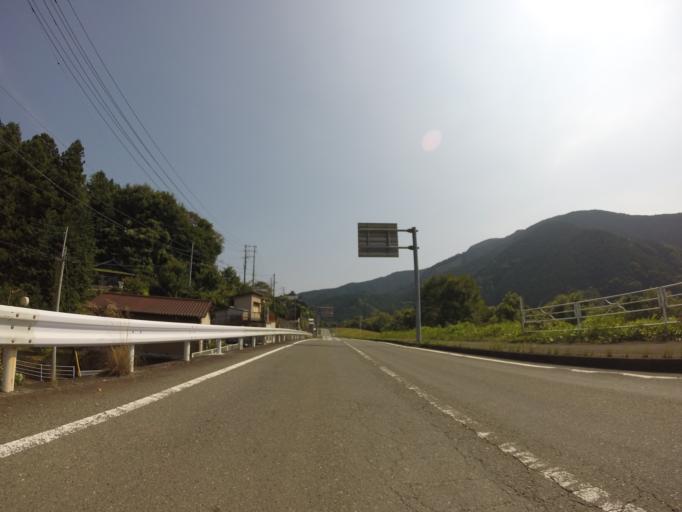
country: JP
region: Shizuoka
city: Shizuoka-shi
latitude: 35.1132
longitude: 138.3611
